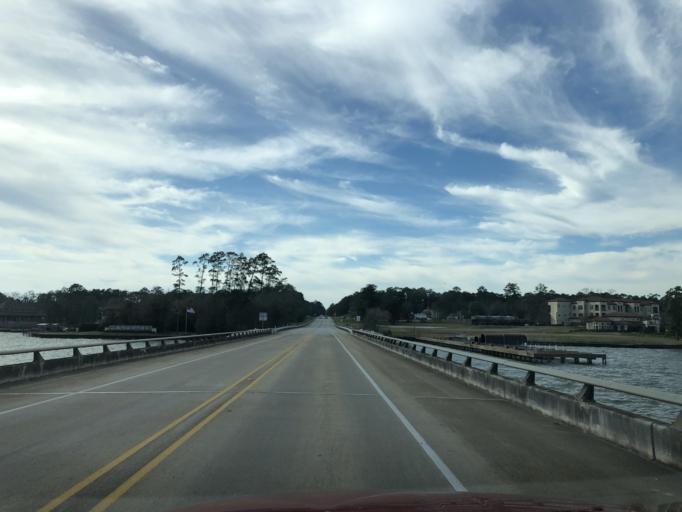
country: US
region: Texas
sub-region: Montgomery County
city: Panorama Village
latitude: 30.4372
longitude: -95.6096
